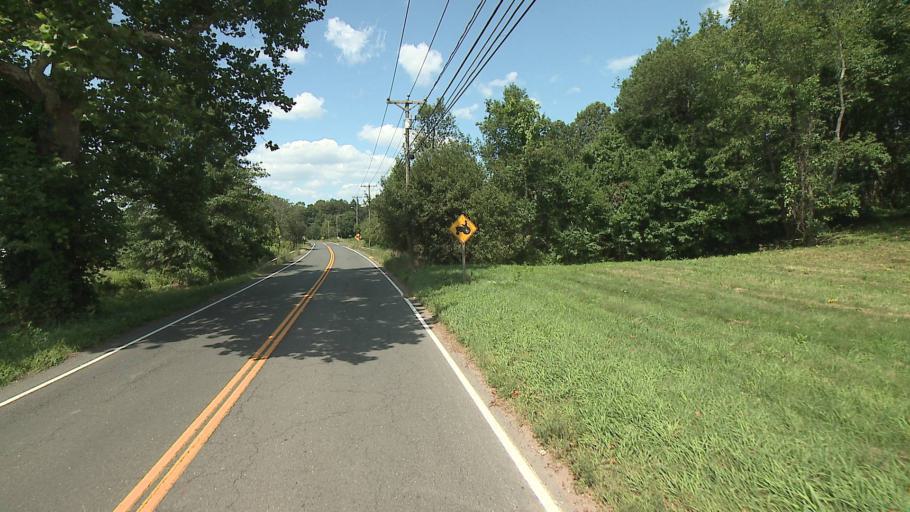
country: US
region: Connecticut
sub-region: Hartford County
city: Broad Brook
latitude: 41.9353
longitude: -72.5119
